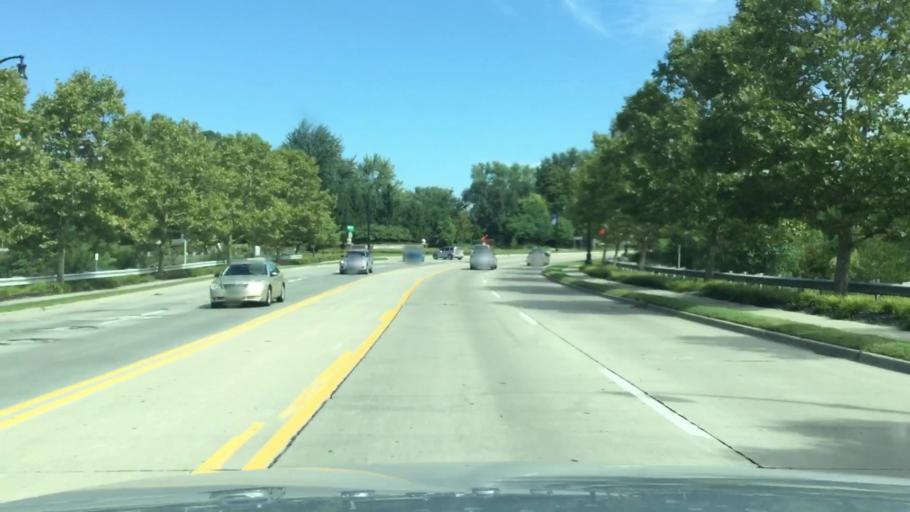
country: US
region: Michigan
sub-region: Wayne County
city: Belleville
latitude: 42.2126
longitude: -83.4923
